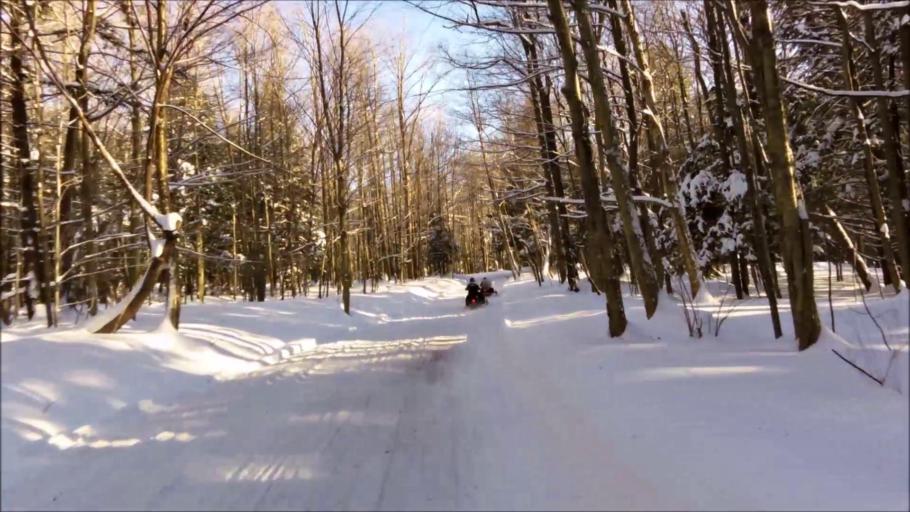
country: US
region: New York
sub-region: Chautauqua County
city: Mayville
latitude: 42.2797
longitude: -79.4075
